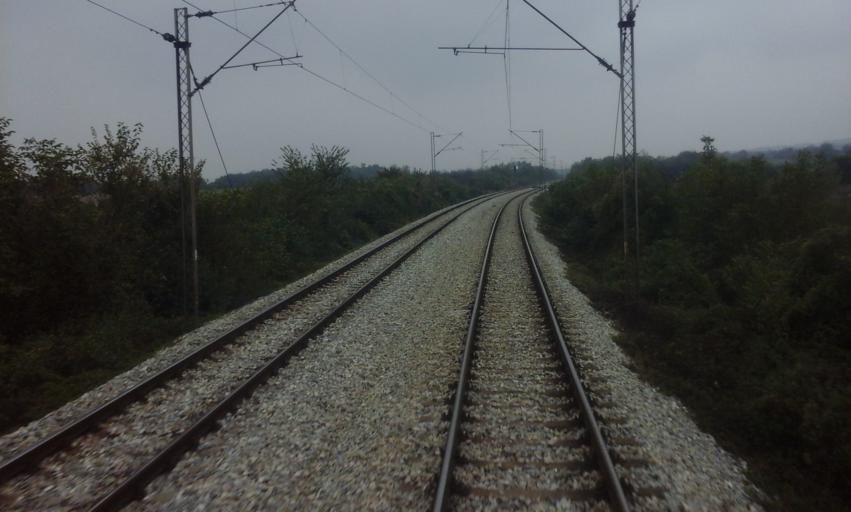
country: RS
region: Central Serbia
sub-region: Sumadijski Okrug
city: Lapovo
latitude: 44.2184
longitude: 21.0948
